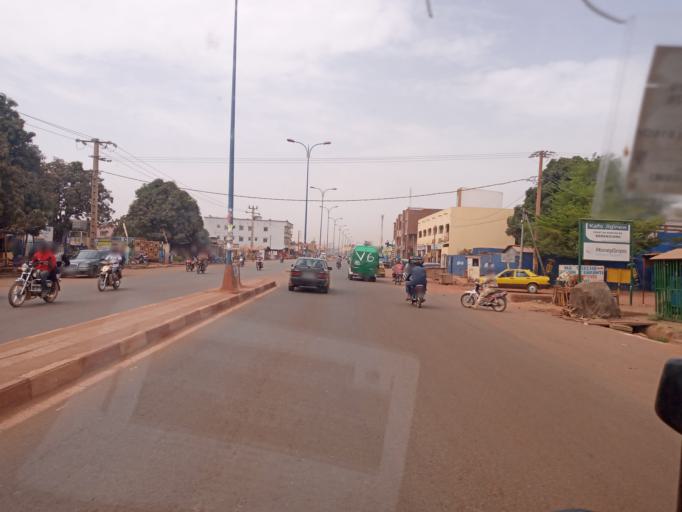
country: ML
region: Bamako
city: Bamako
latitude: 12.6001
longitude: -8.0537
